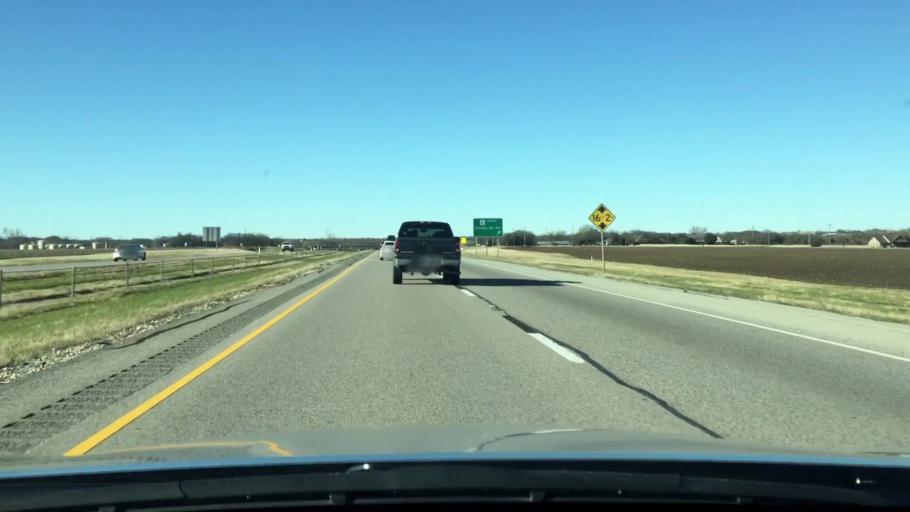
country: US
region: Texas
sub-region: Johnson County
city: Grandview
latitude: 32.2820
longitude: -97.1751
